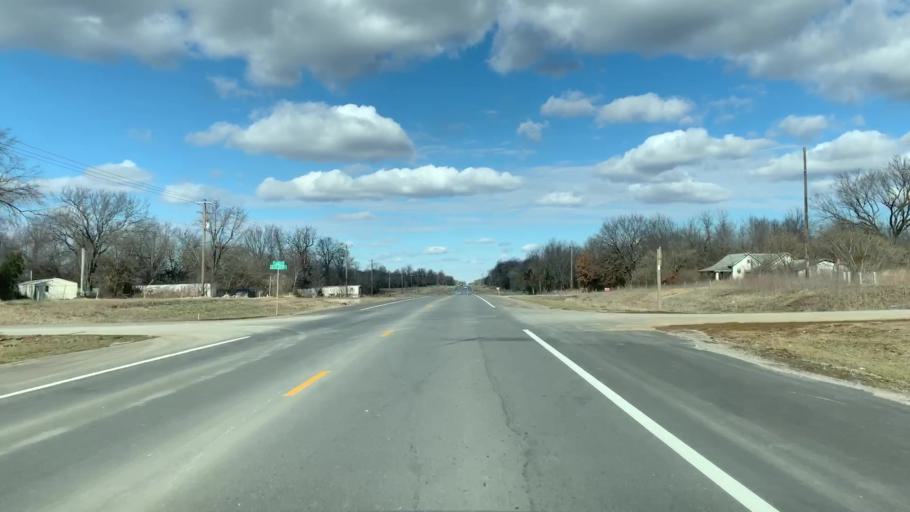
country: US
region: Kansas
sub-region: Cherokee County
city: Columbus
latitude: 37.2223
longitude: -94.8319
